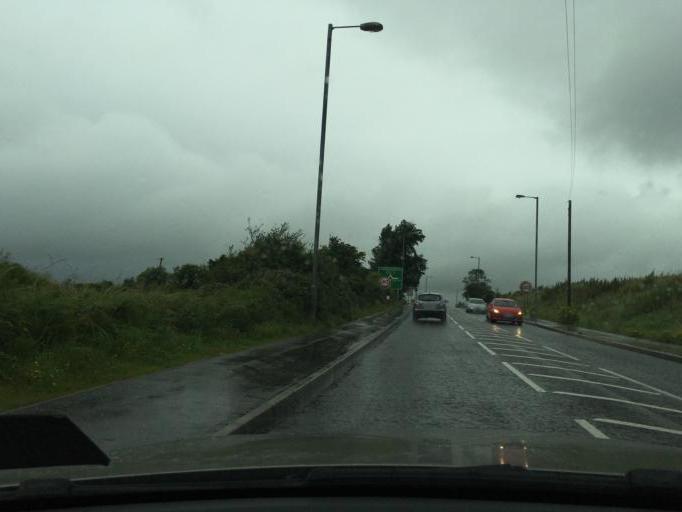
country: GB
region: Northern Ireland
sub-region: Fermanagh District
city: Enniskillen
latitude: 54.3580
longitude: -7.6360
